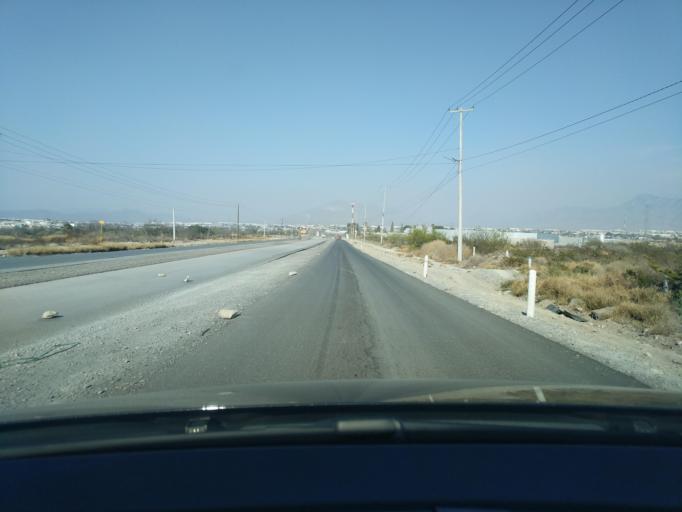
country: MX
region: Coahuila
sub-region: Ramos Arizpe
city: Ramos Arizpe
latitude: 25.5351
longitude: -100.9738
